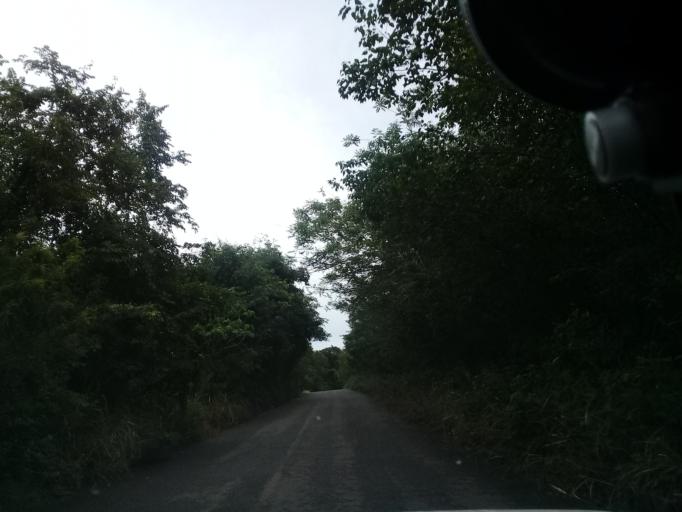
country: MX
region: Hidalgo
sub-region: Huejutla de Reyes
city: Chalahuiyapa
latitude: 21.2006
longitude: -98.3453
